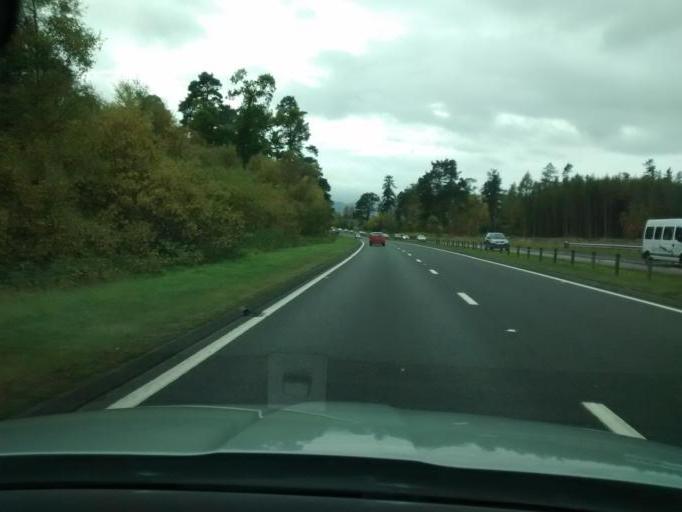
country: GB
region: Scotland
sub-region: Perth and Kinross
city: Methven
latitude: 56.3657
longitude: -3.5537
